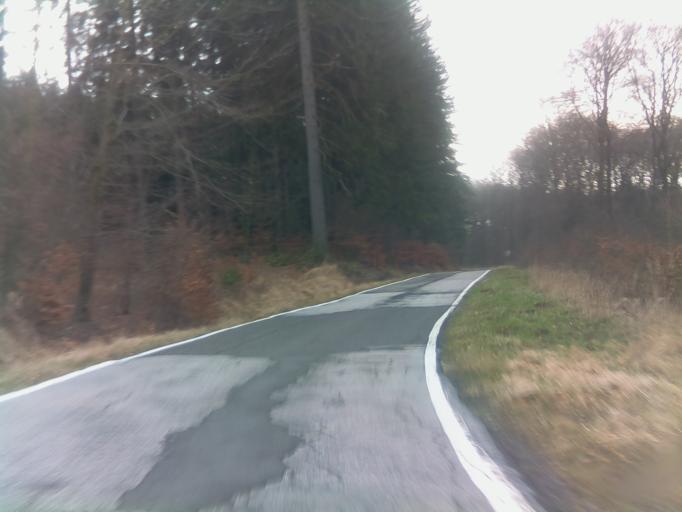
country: DE
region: Rheinland-Pfalz
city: Oberheimbach
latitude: 49.9938
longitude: 7.7734
